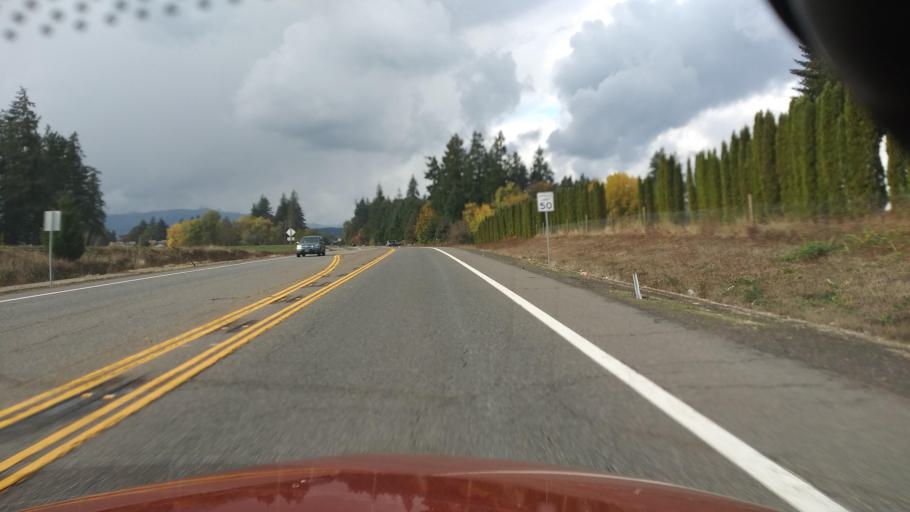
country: US
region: Oregon
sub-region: Washington County
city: Forest Grove
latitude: 45.5287
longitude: -123.0881
